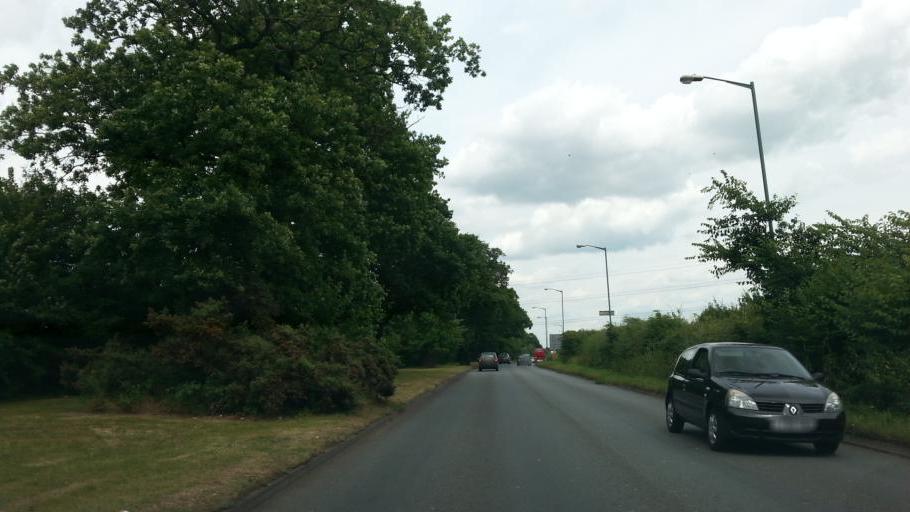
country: GB
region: England
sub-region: Solihull
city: Chelmsley Wood
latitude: 52.4759
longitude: -1.7204
